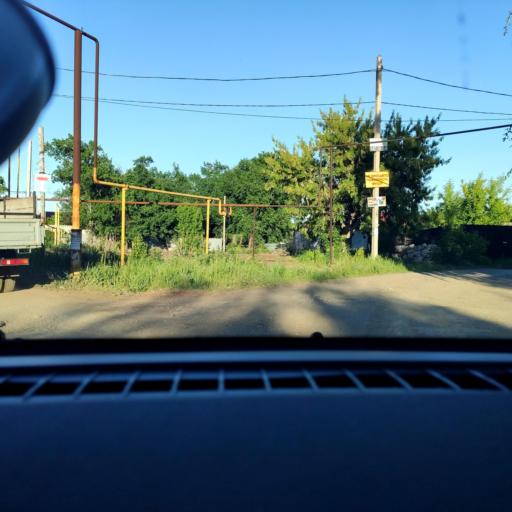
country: RU
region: Samara
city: Samara
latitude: 53.1300
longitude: 50.1806
